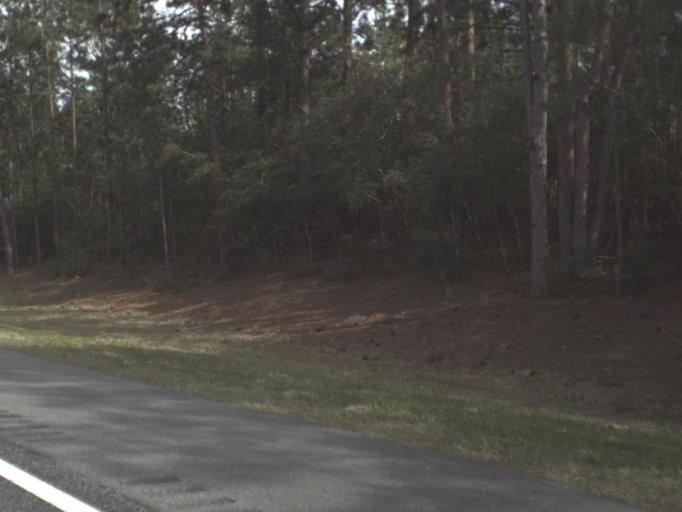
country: US
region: Florida
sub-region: Walton County
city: DeFuniak Springs
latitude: 30.6907
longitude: -86.0549
